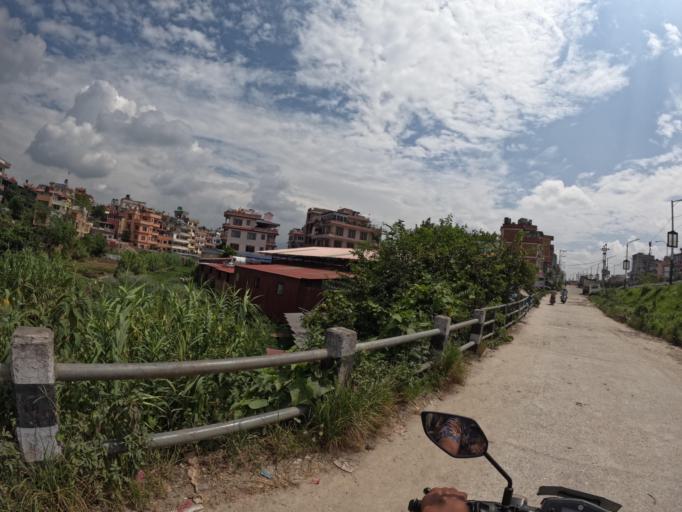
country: NP
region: Central Region
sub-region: Bagmati Zone
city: Patan
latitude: 27.6750
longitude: 85.3617
